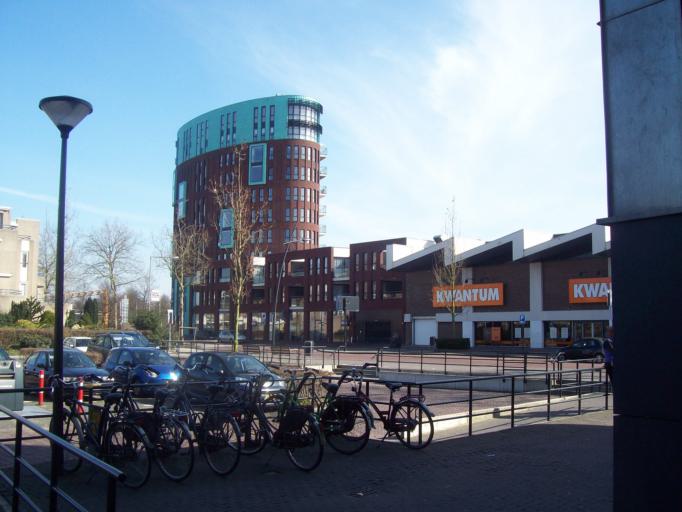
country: NL
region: North Brabant
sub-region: Gemeente Uden
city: Uden
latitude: 51.6601
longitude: 5.6155
